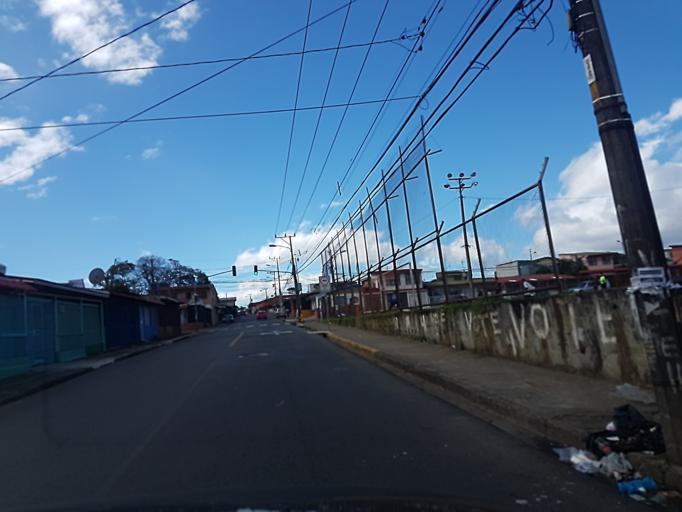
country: CR
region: San Jose
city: San Felipe
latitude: 9.9196
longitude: -84.0961
